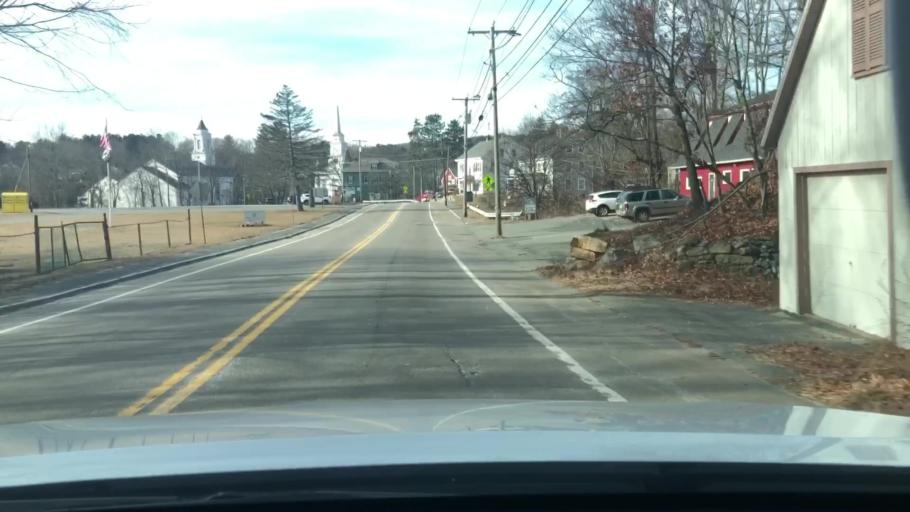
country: US
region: Massachusetts
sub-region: Worcester County
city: Upton
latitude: 42.1737
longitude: -71.6000
